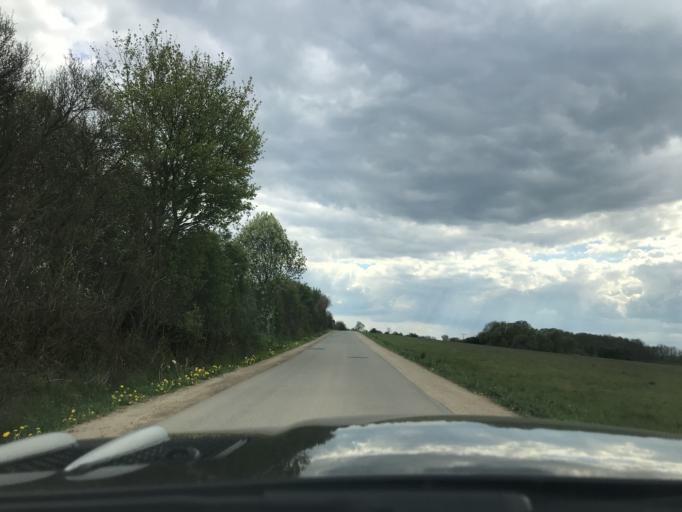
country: DE
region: Schleswig-Holstein
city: Gross Gronau
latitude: 53.7867
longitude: 10.7850
